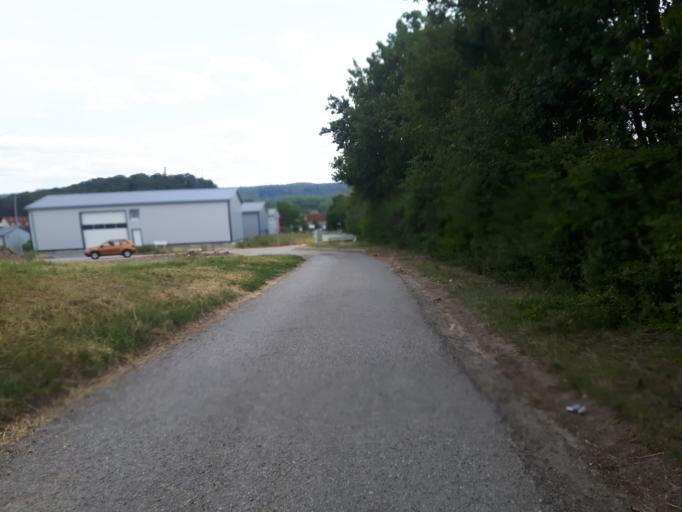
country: DE
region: Baden-Wuerttemberg
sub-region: Regierungsbezirk Stuttgart
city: Zaberfeld
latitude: 49.0650
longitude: 8.9301
